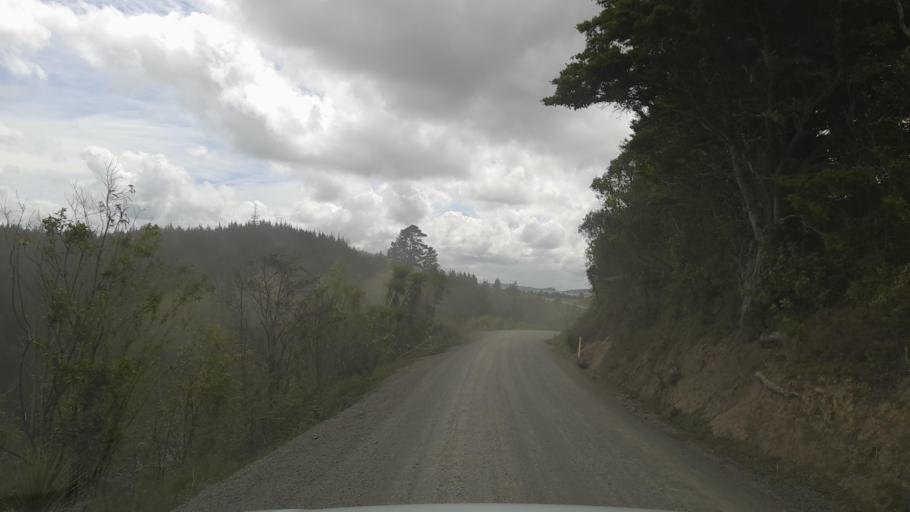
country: NZ
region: Auckland
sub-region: Auckland
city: Wellsford
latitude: -36.1624
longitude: 174.3546
